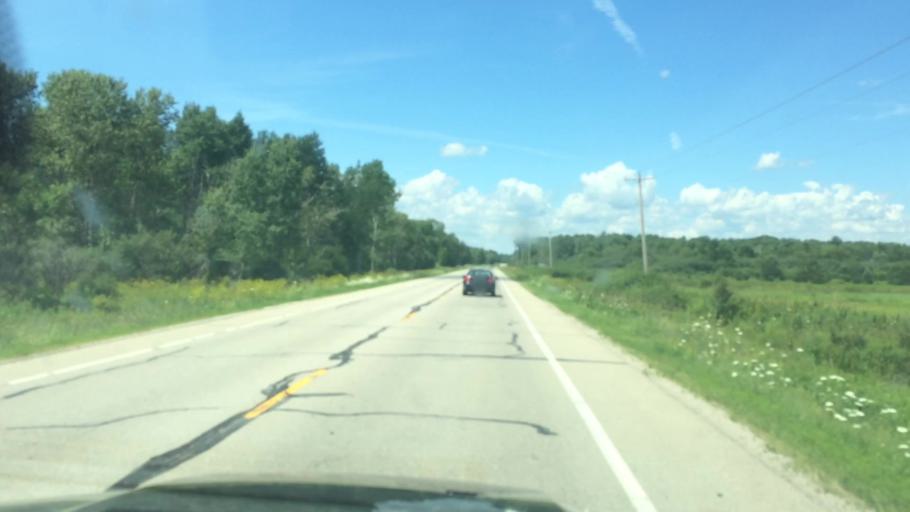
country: US
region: Wisconsin
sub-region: Marinette County
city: Peshtigo
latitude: 45.1001
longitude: -87.7174
